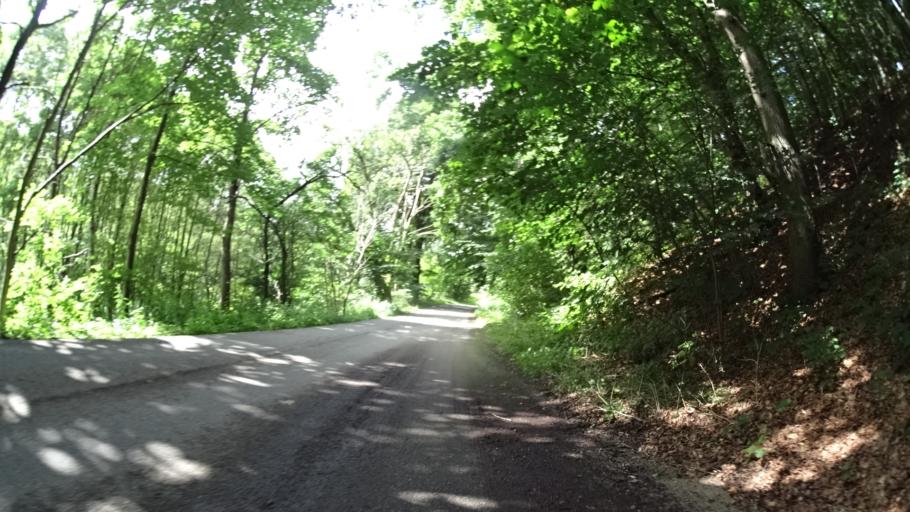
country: DK
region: Central Jutland
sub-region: Skanderborg Kommune
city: Horning
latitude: 56.1079
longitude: 10.0127
